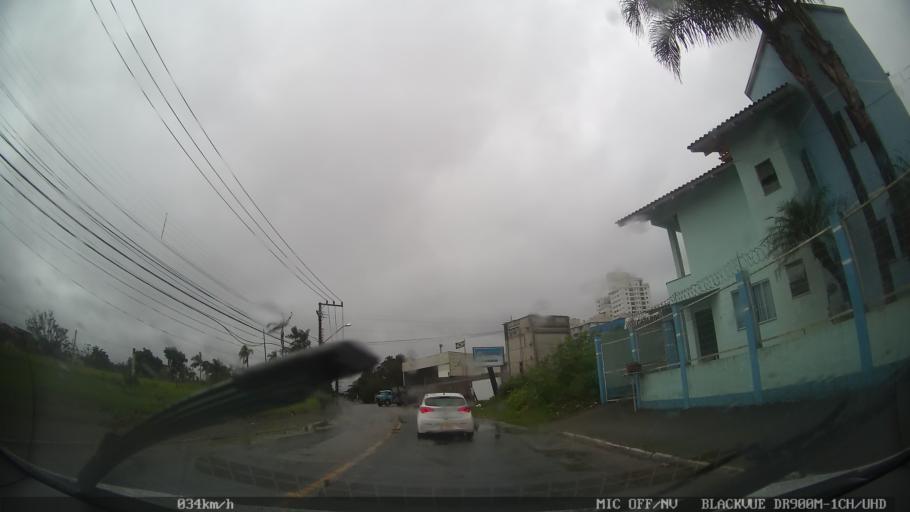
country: BR
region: Santa Catarina
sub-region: Itajai
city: Itajai
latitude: -26.9276
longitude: -48.6839
